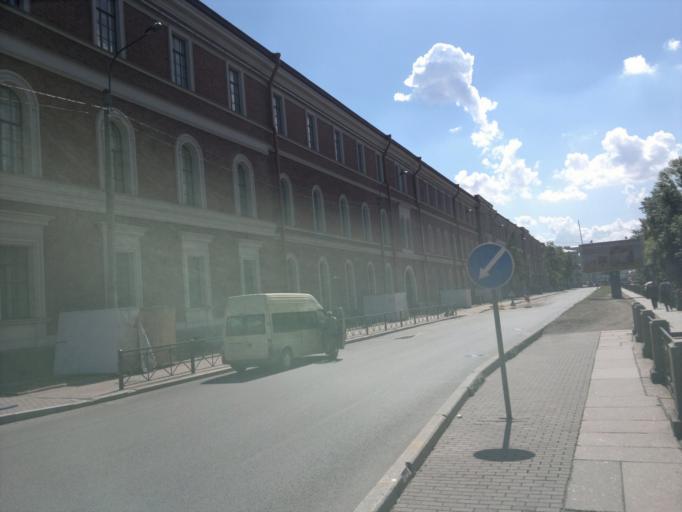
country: RU
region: St.-Petersburg
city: Saint Petersburg
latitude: 59.9307
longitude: 30.2925
